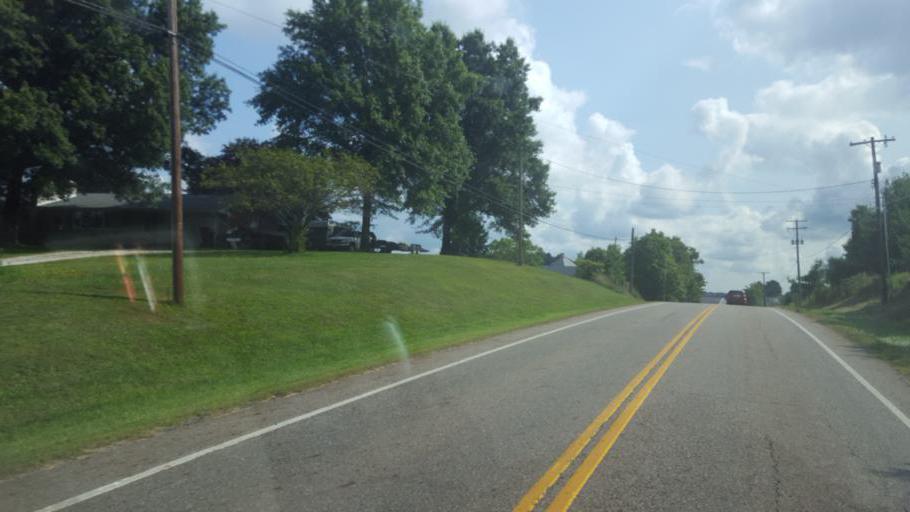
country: US
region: Ohio
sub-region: Stark County
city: East Canton
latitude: 40.7961
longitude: -81.2438
